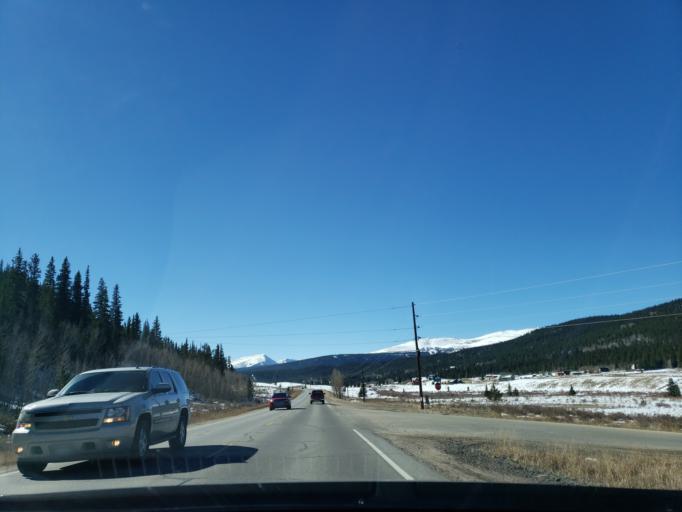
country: US
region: Colorado
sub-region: Park County
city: Fairplay
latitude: 39.3126
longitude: -106.0593
